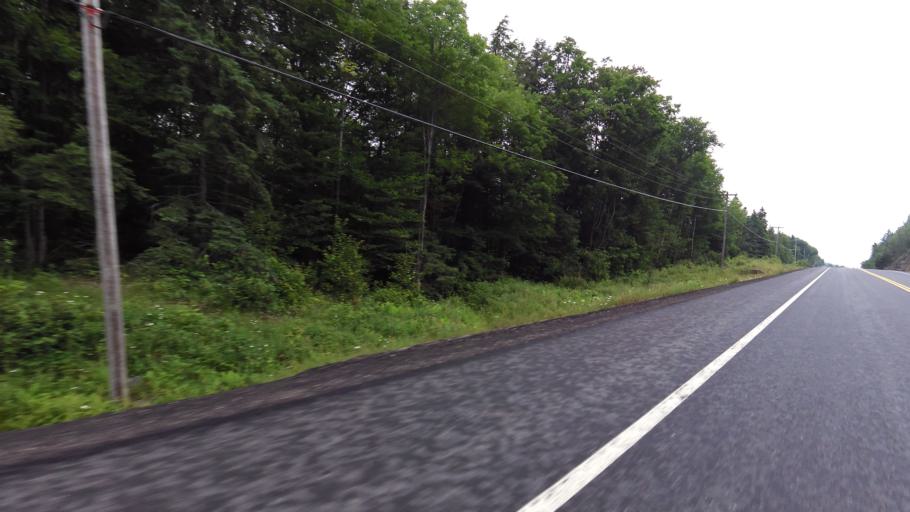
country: CA
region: Ontario
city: Huntsville
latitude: 45.5060
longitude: -78.7276
